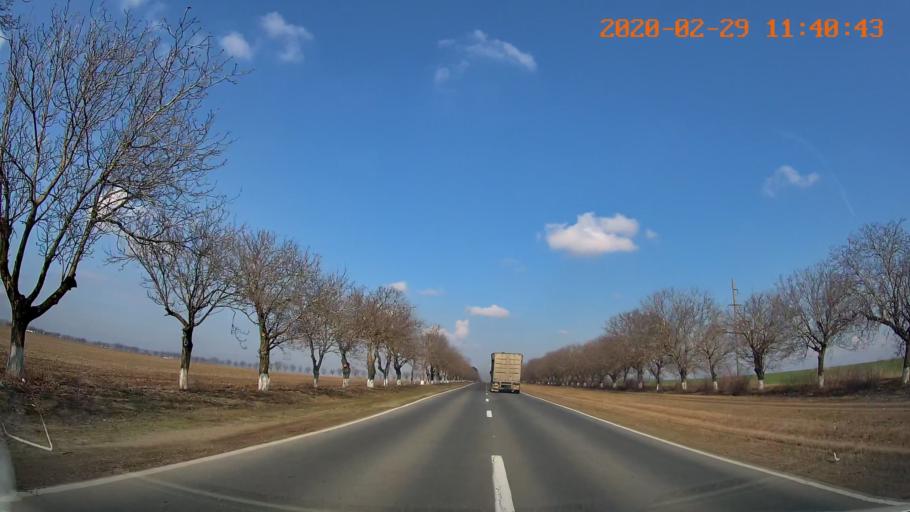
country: MD
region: Rezina
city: Saharna
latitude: 47.6607
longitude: 29.0191
